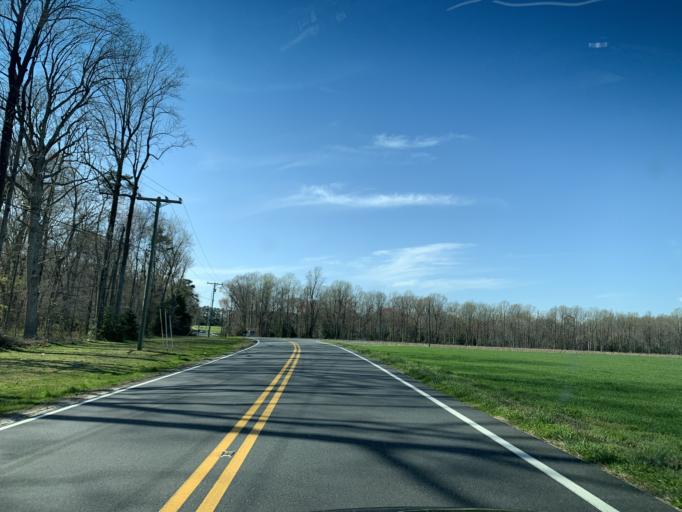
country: US
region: Delaware
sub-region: Kent County
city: Riverview
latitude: 38.9635
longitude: -75.4830
